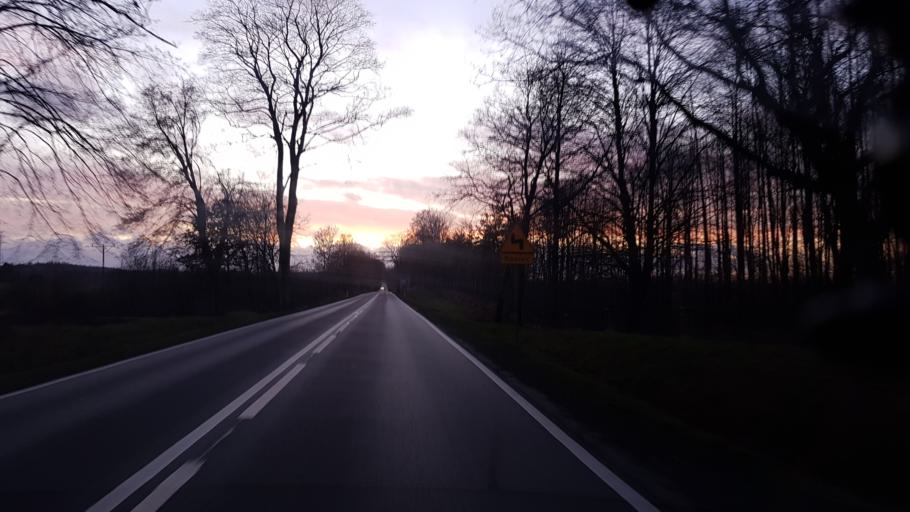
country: PL
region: Pomeranian Voivodeship
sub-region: Powiat bytowski
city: Tuchomie
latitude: 54.1275
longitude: 17.3822
